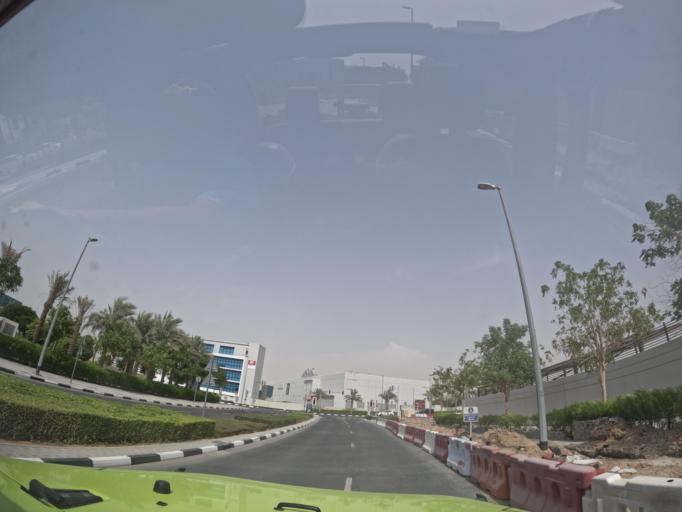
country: AE
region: Dubai
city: Dubai
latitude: 25.1181
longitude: 55.3806
